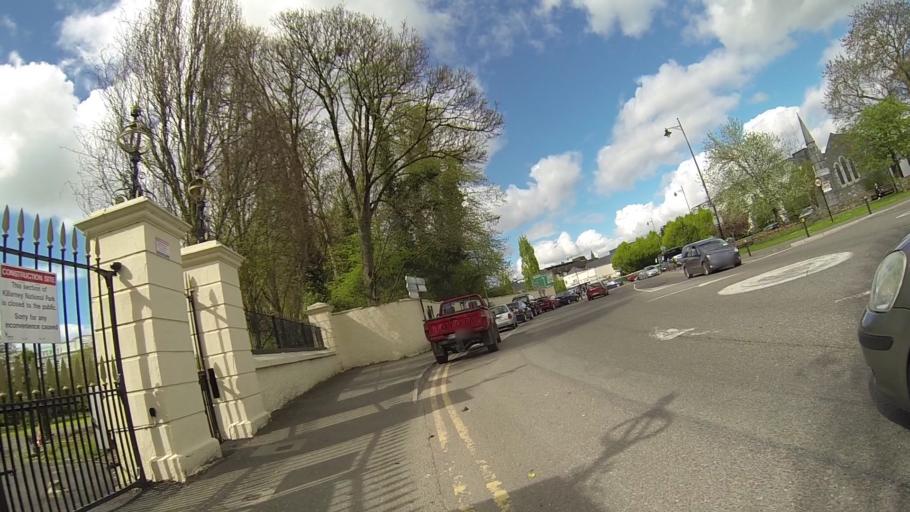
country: IE
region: Munster
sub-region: Ciarrai
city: Cill Airne
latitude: 52.0568
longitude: -9.5072
